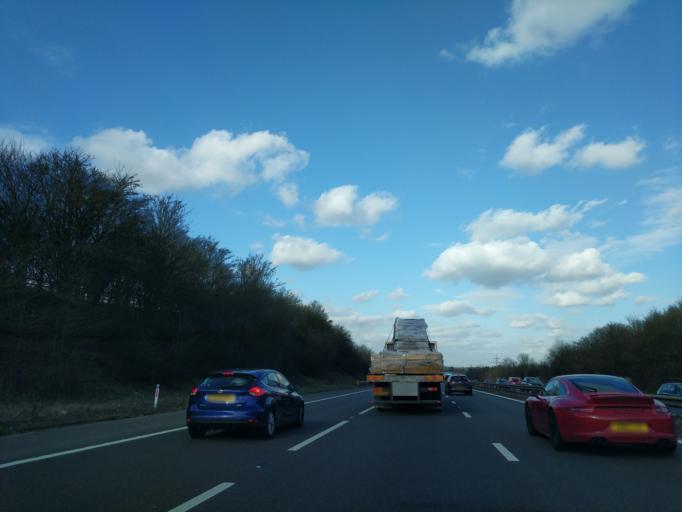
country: GB
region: England
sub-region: Hertfordshire
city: Letchworth Garden City
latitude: 51.9495
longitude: -0.2115
